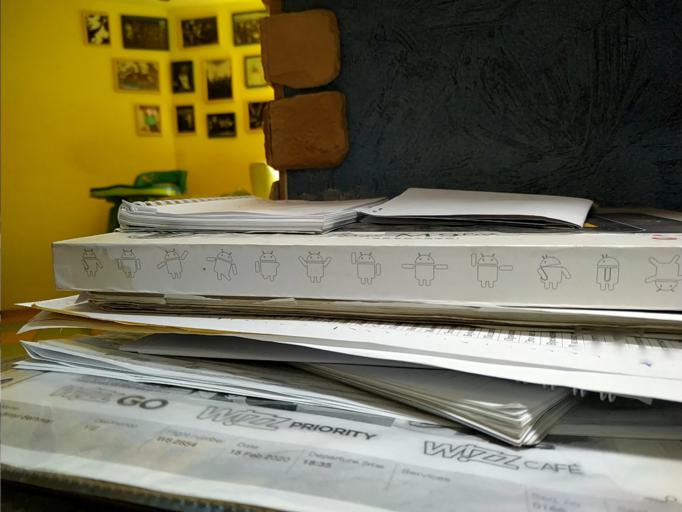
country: RU
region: Novgorod
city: Utorgosh
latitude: 58.2249
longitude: 29.9369
